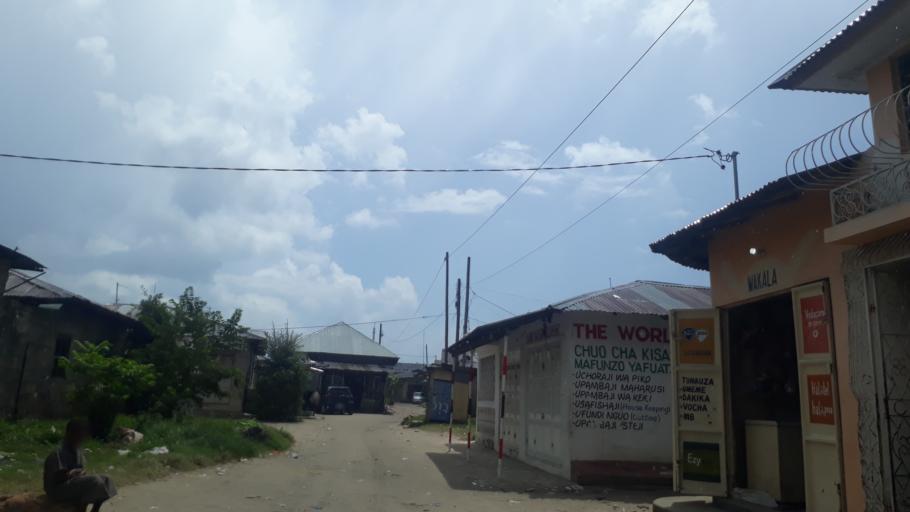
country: TZ
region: Zanzibar Urban/West
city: Zanzibar
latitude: -6.1773
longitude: 39.2099
